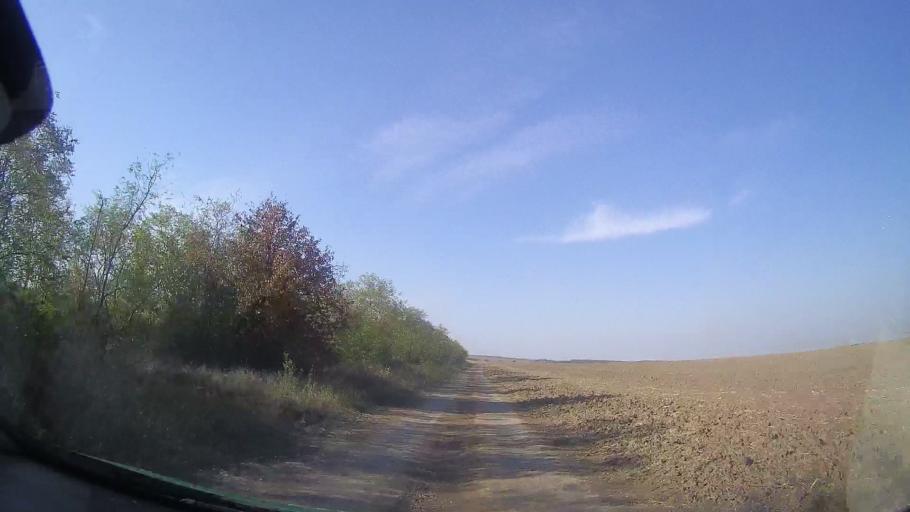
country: RO
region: Timis
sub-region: Comuna Bogda
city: Bogda
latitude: 45.8973
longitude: 21.5667
